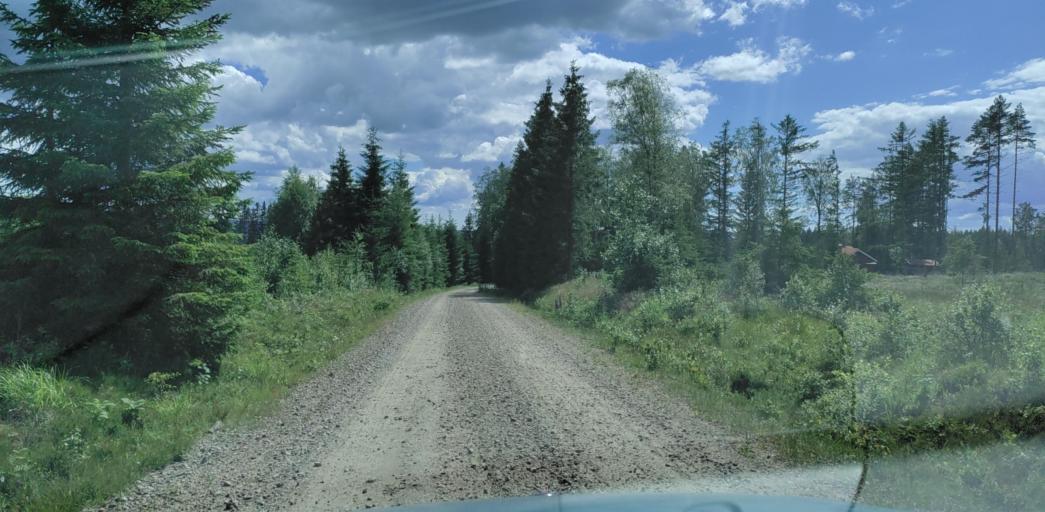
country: SE
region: Vaermland
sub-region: Hagfors Kommun
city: Ekshaerad
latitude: 60.0492
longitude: 13.3094
